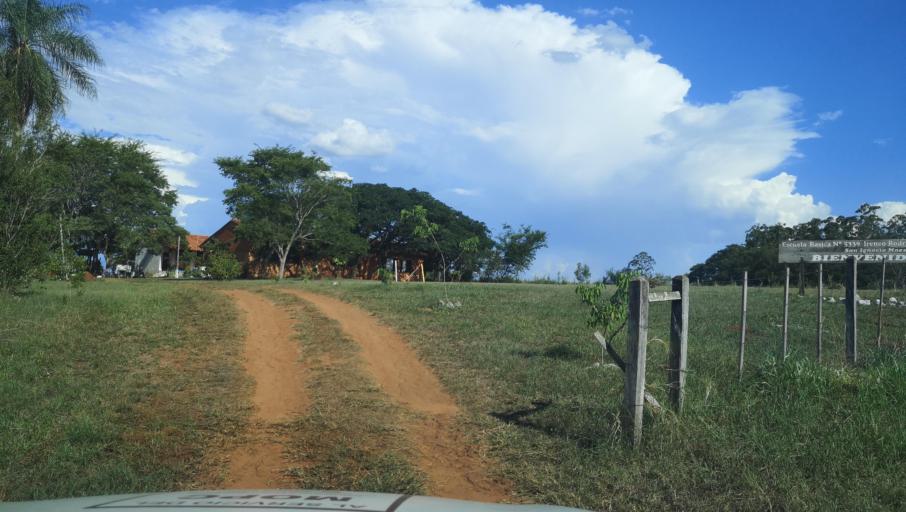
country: PY
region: Misiones
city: Santa Maria
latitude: -26.8951
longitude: -57.0214
